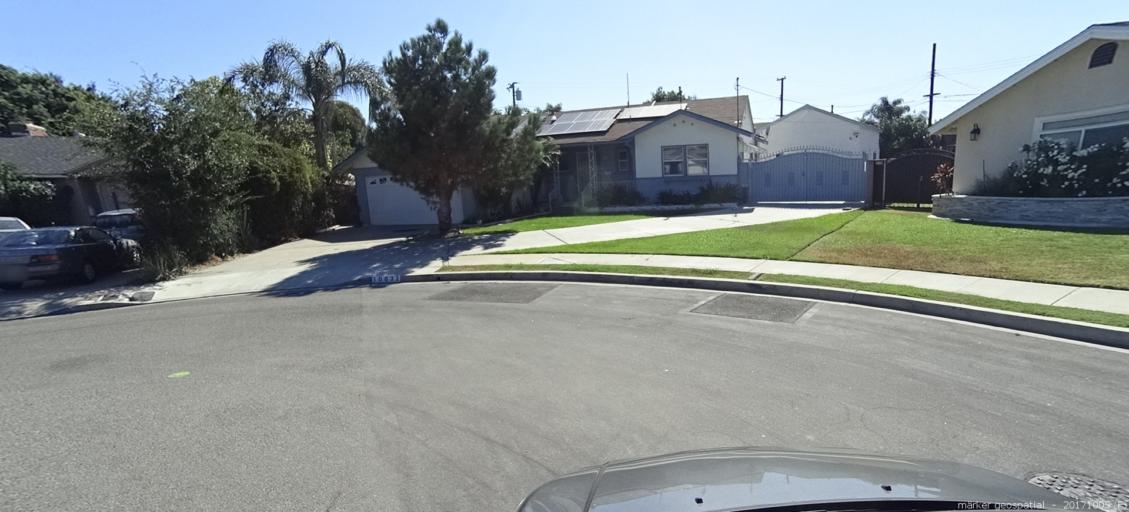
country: US
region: California
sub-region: Orange County
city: Garden Grove
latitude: 33.7873
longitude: -117.9473
